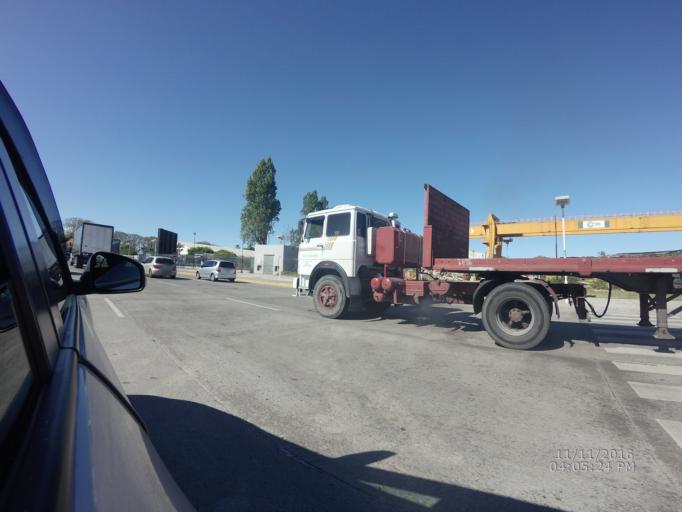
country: AR
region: Buenos Aires F.D.
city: Retiro
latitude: -34.5665
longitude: -58.4010
